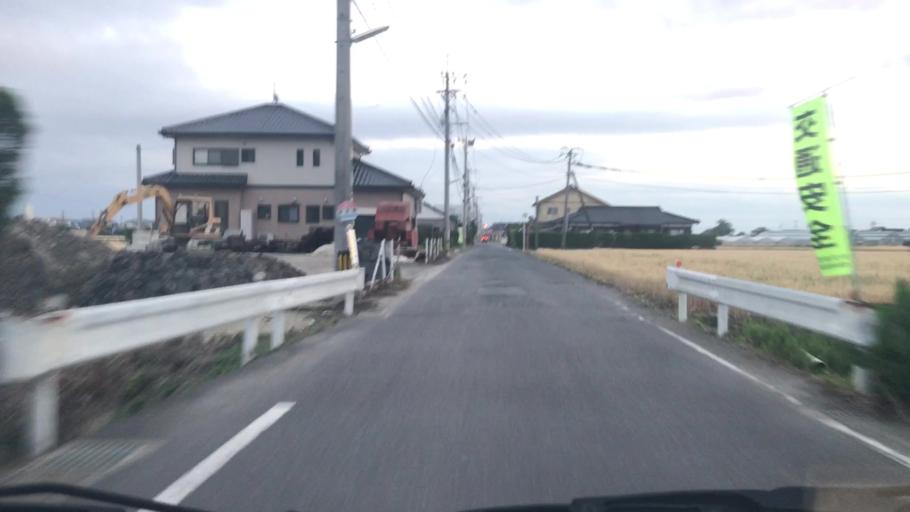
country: JP
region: Saga Prefecture
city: Saga-shi
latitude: 33.2308
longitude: 130.3019
